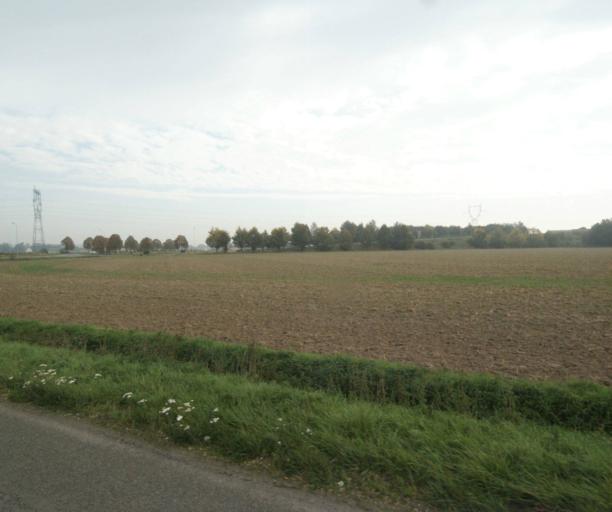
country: FR
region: Nord-Pas-de-Calais
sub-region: Departement du Nord
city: Phalempin
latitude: 50.5330
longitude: 3.0145
